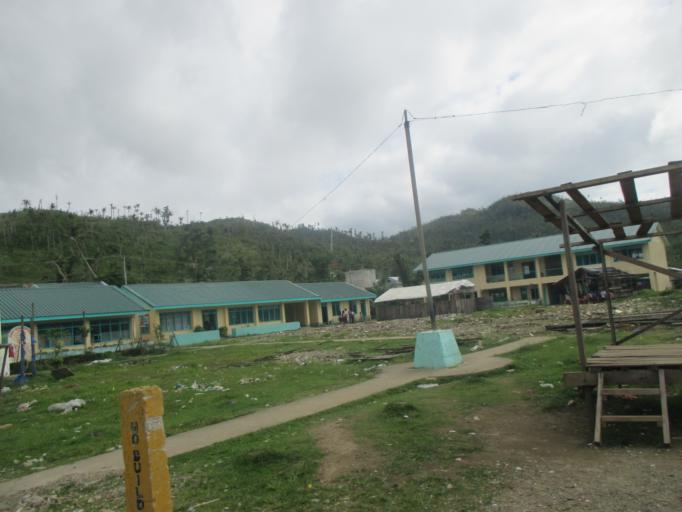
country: PH
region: Eastern Visayas
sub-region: Province of Eastern Samar
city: Lawa-an
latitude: 11.1080
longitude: 125.2128
